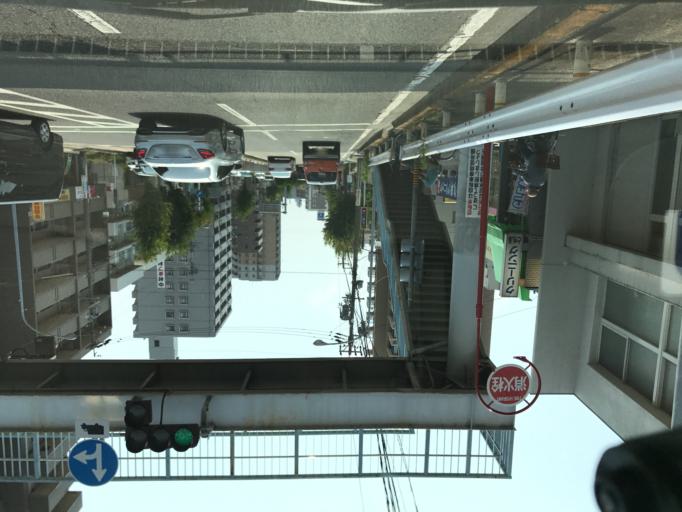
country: JP
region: Aichi
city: Nagoya-shi
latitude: 35.1183
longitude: 136.9508
